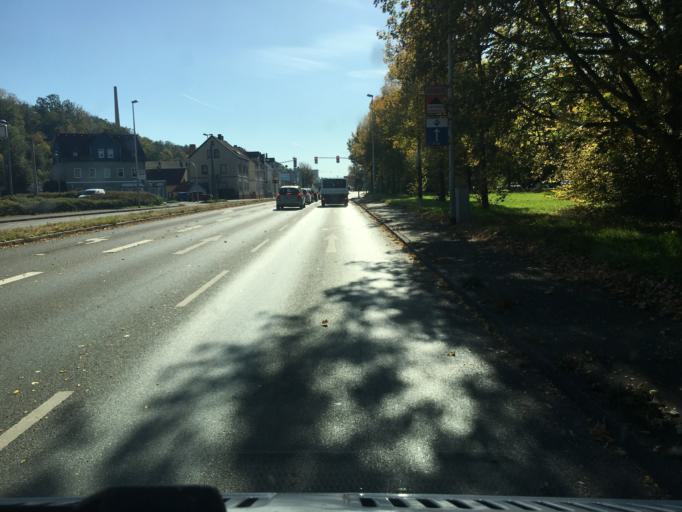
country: DE
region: Saxony
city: Zwickau
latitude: 50.7311
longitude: 12.4992
